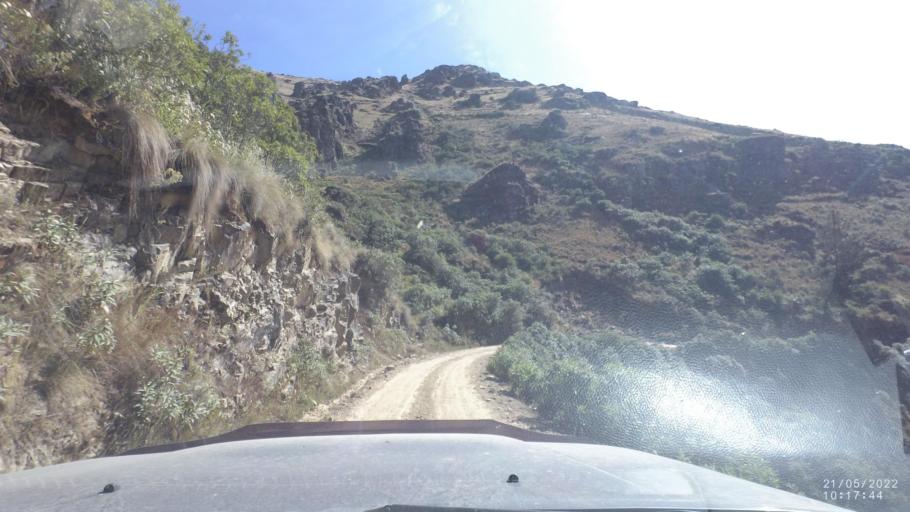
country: BO
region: Cochabamba
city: Colomi
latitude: -17.3281
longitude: -65.9631
